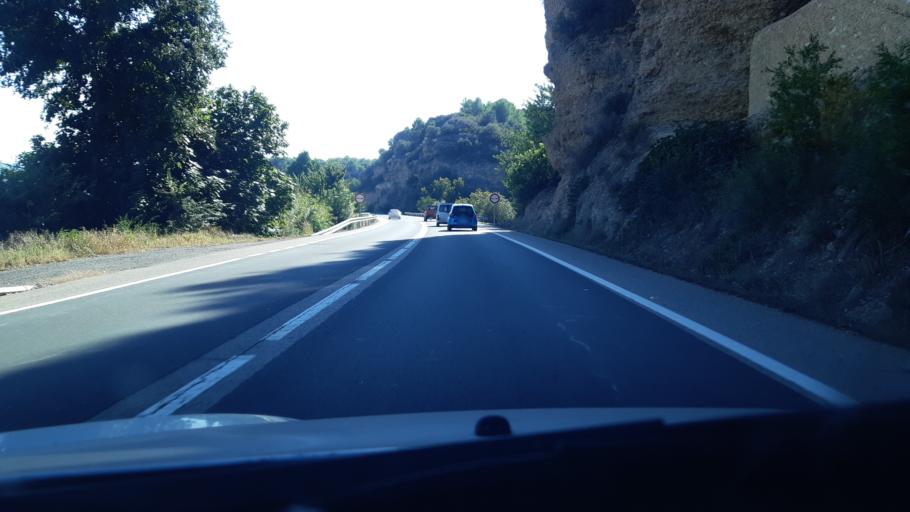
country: ES
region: Catalonia
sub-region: Provincia de Tarragona
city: Tivenys
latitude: 40.8724
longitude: 0.5012
